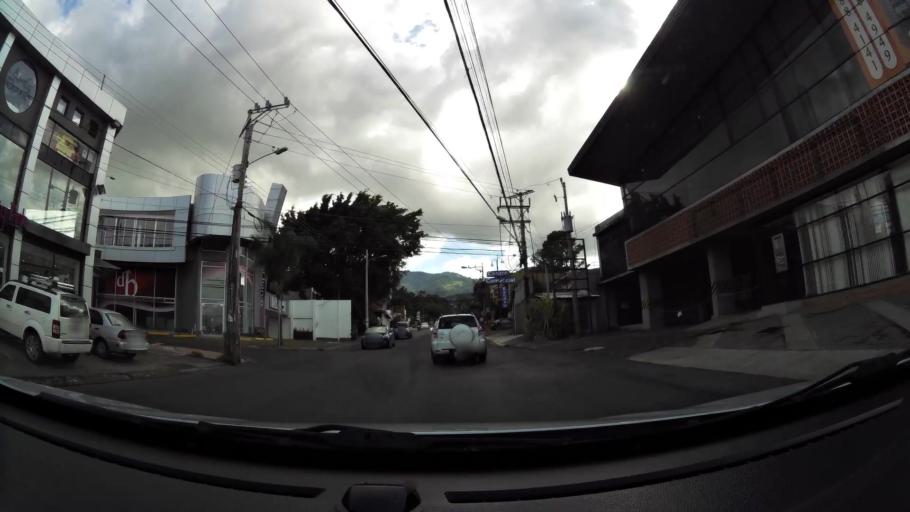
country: CR
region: San Jose
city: San Rafael
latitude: 9.9289
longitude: -84.1335
